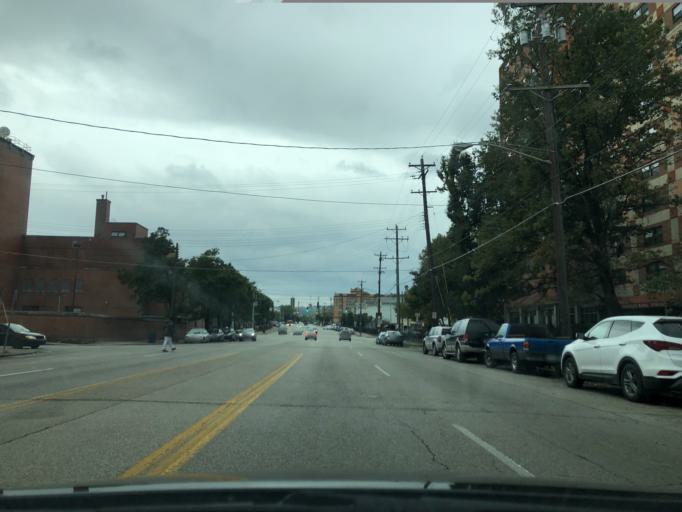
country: US
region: Kentucky
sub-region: Kenton County
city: Ludlow
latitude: 39.1147
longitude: -84.5274
